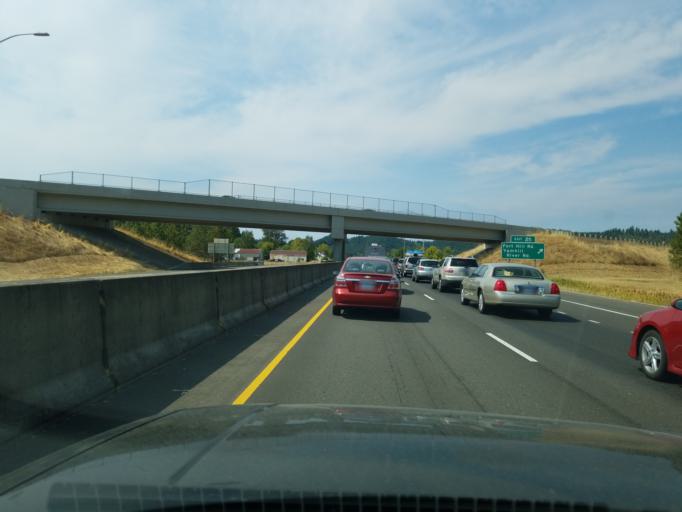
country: US
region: Oregon
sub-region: Yamhill County
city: Willamina
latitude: 45.0543
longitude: -123.5410
